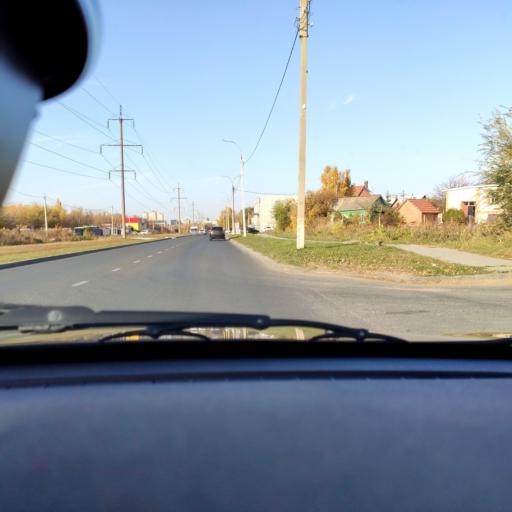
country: RU
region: Samara
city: Tol'yatti
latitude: 53.5187
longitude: 49.3957
